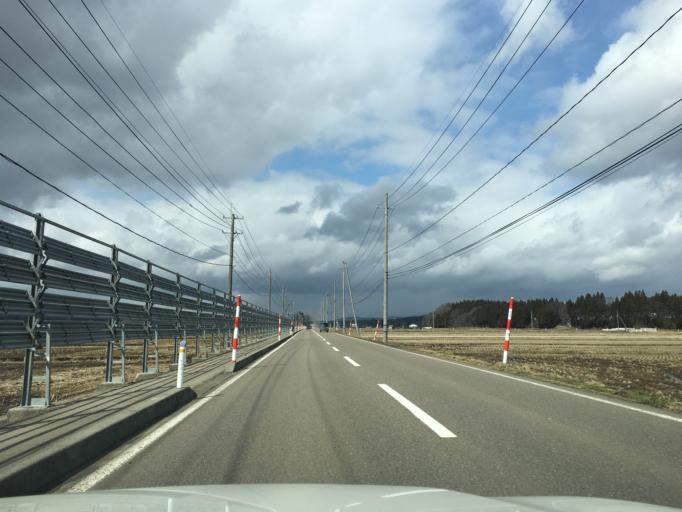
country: JP
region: Akita
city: Takanosu
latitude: 40.1278
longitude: 140.3636
